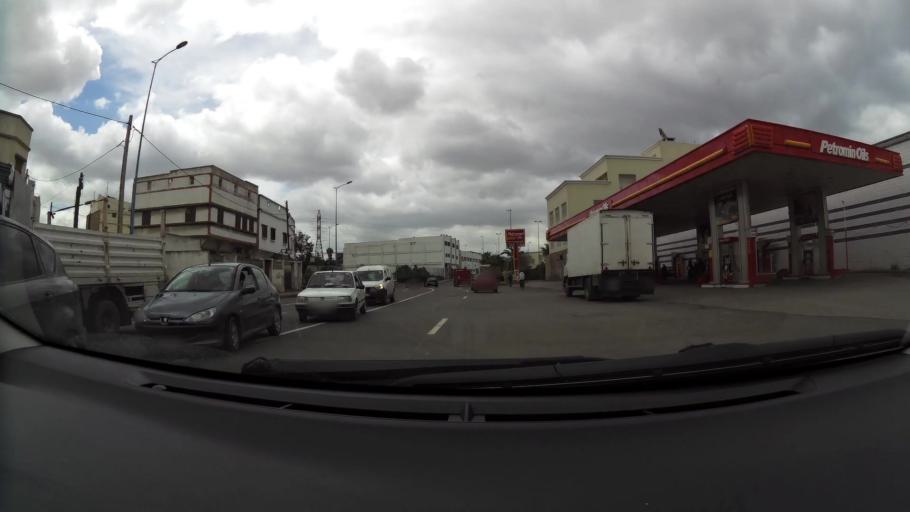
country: MA
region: Grand Casablanca
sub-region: Casablanca
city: Casablanca
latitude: 33.6018
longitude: -7.5450
